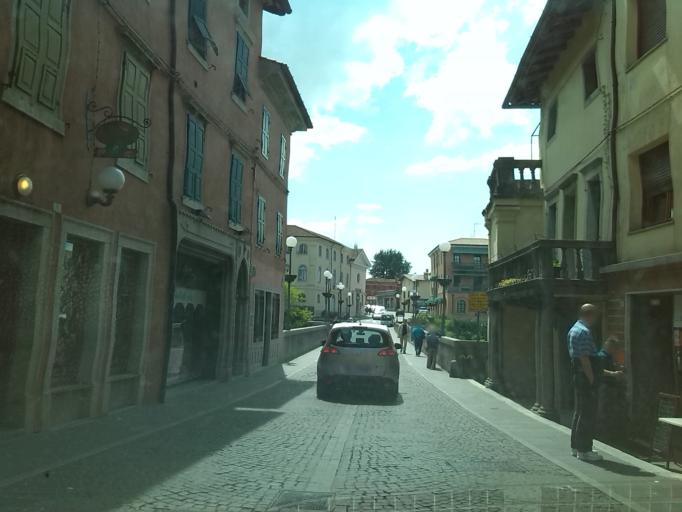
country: IT
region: Friuli Venezia Giulia
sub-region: Provincia di Udine
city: Cividale del Friuli
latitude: 46.0923
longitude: 13.4315
